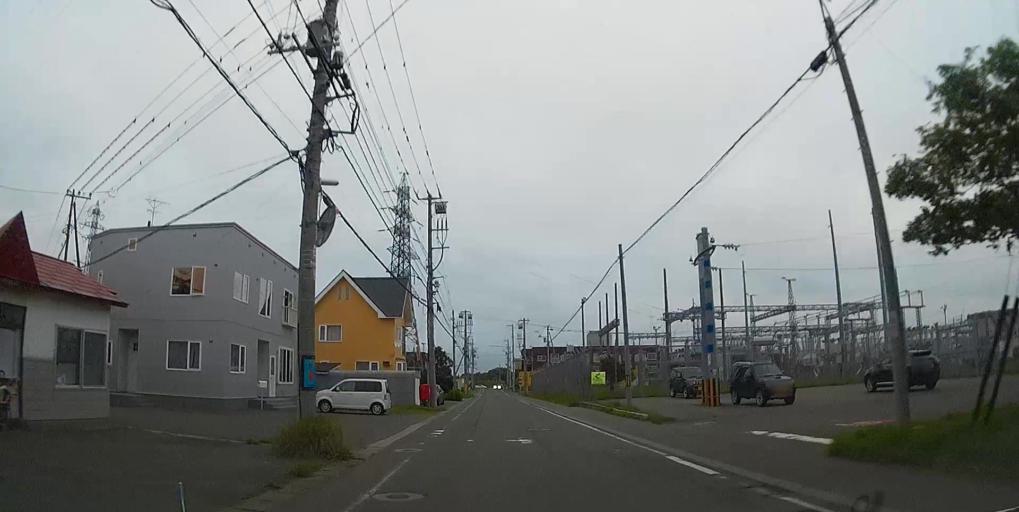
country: JP
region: Hokkaido
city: Nanae
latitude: 42.2600
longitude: 140.2725
